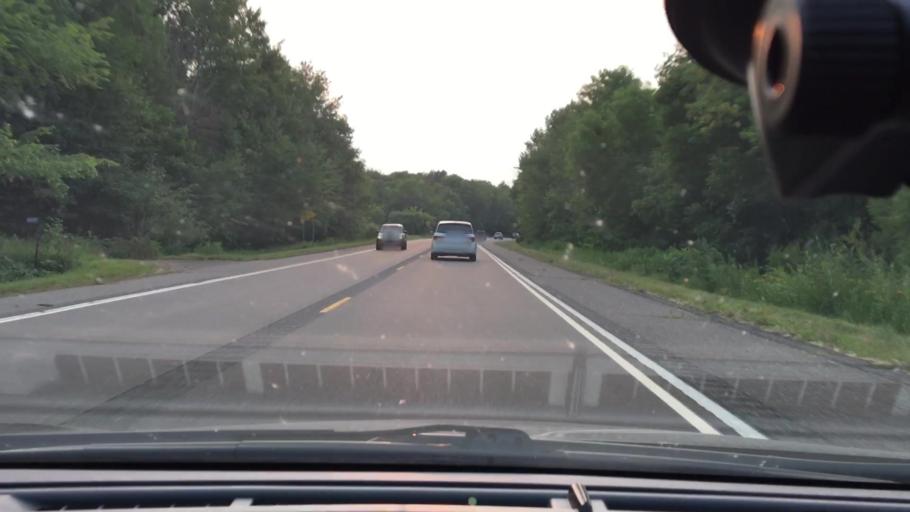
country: US
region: Minnesota
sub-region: Mille Lacs County
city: Vineland
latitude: 46.1294
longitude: -93.6818
